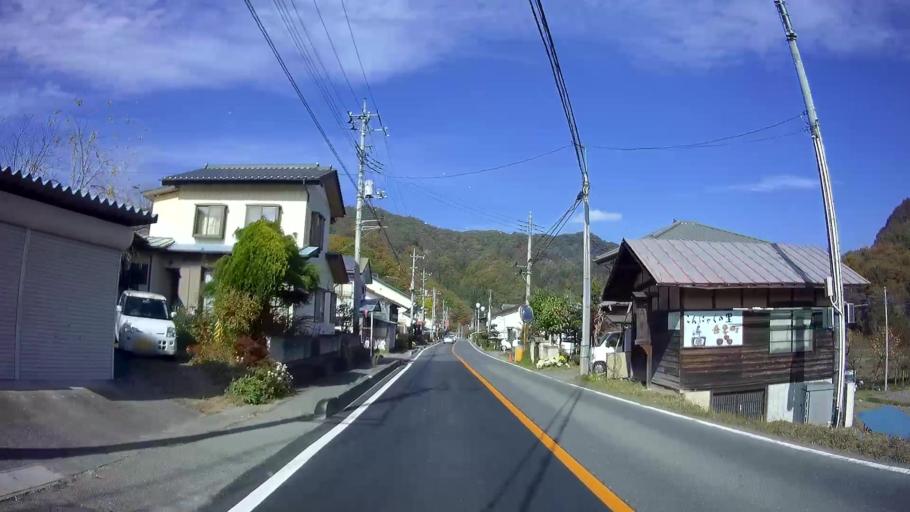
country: JP
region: Gunma
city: Nakanojomachi
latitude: 36.5099
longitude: 138.7754
